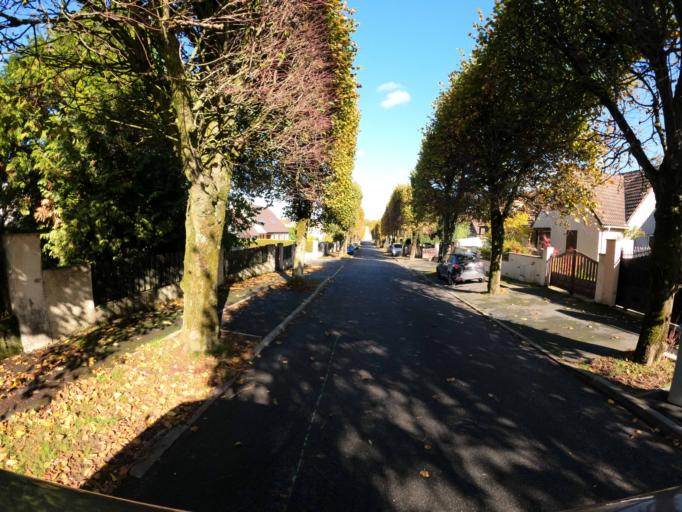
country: FR
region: Ile-de-France
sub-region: Departement de Seine-et-Marne
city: Esbly
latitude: 48.8969
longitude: 2.8086
